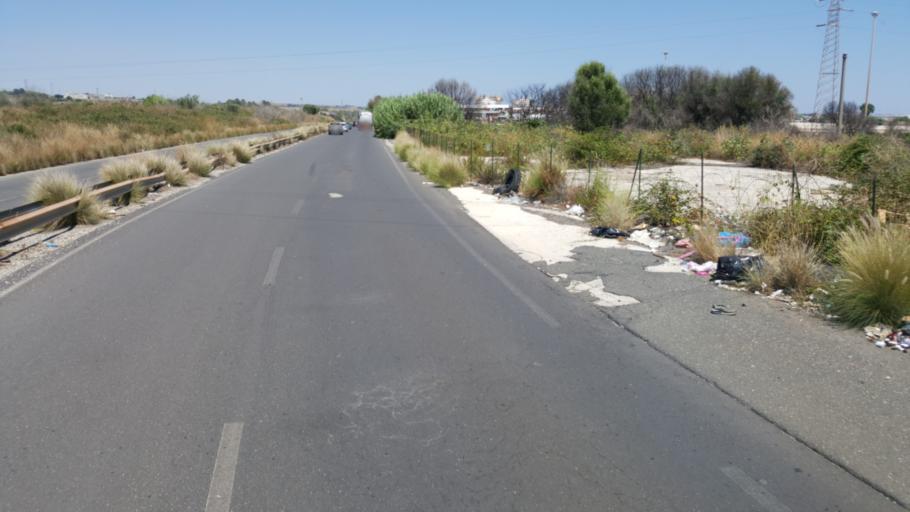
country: IT
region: Sicily
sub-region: Provincia di Siracusa
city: Melilli
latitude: 37.2037
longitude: 15.1606
